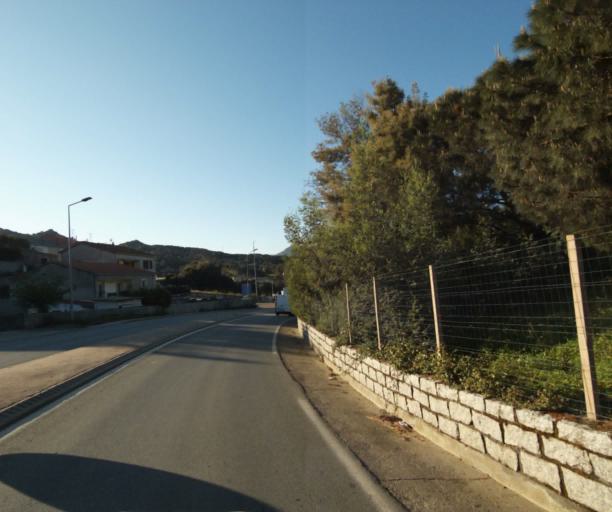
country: FR
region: Corsica
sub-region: Departement de la Corse-du-Sud
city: Propriano
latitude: 41.6687
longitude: 8.9210
